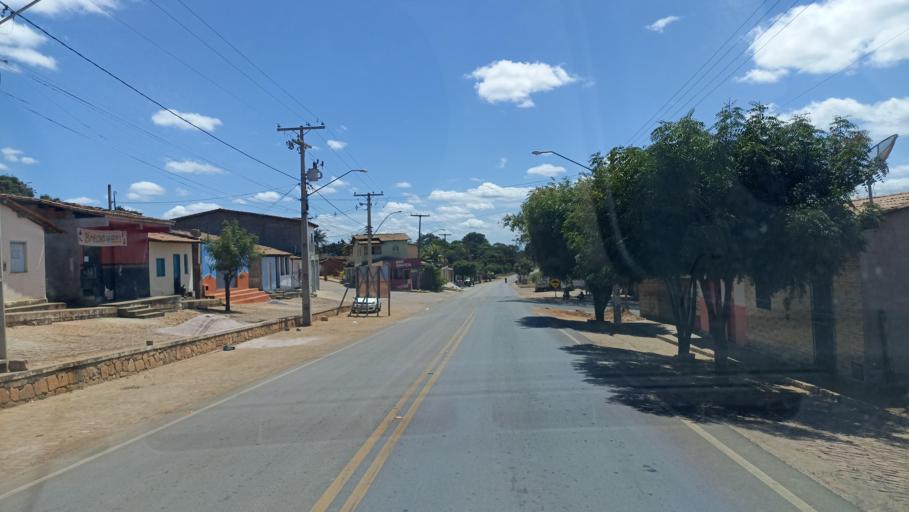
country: BR
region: Bahia
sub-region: Andarai
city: Vera Cruz
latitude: -12.7931
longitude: -41.3283
